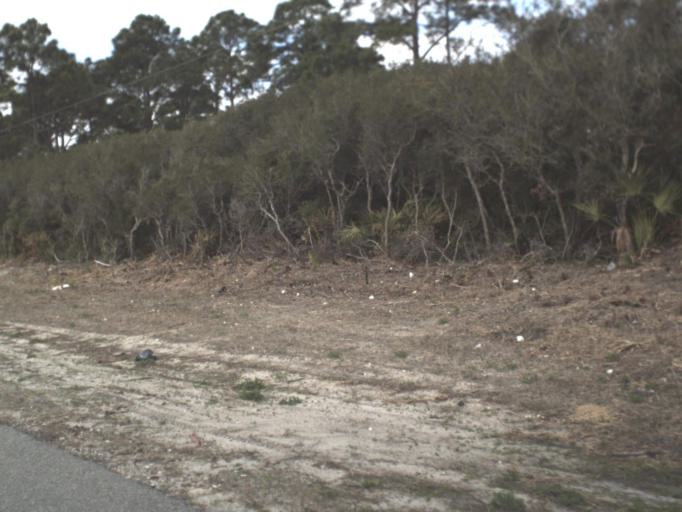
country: US
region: Florida
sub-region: Franklin County
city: Eastpoint
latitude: 29.7746
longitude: -84.7902
